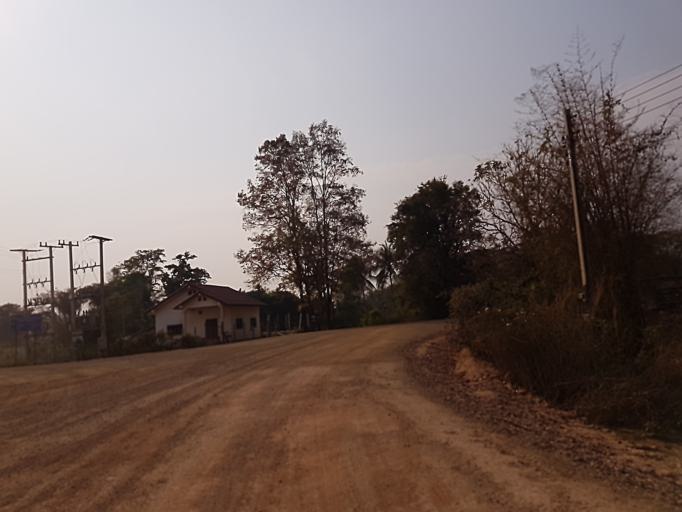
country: TH
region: Nong Khai
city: Phon Phisai
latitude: 18.0005
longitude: 102.9090
